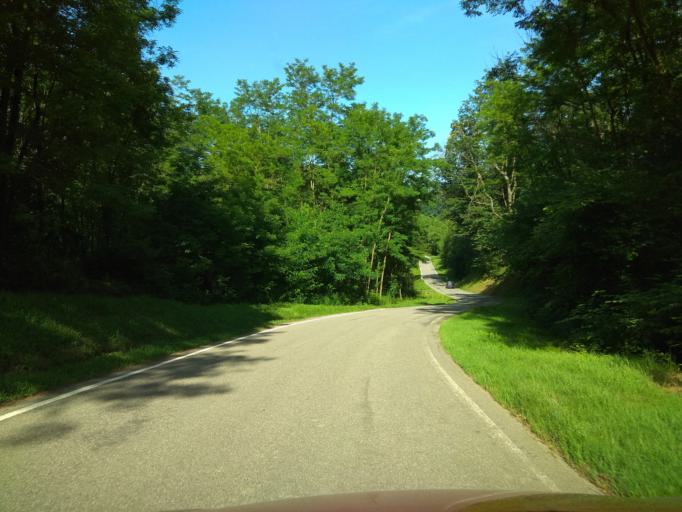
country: IT
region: Piedmont
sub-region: Provincia di Vercelli
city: Roasio
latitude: 45.6058
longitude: 8.2798
